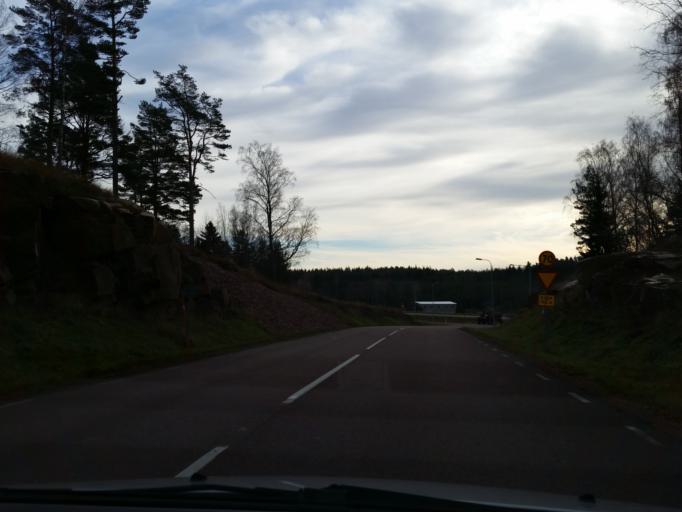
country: AX
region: Alands landsbygd
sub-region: Saltvik
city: Saltvik
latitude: 60.2476
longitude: 20.0404
